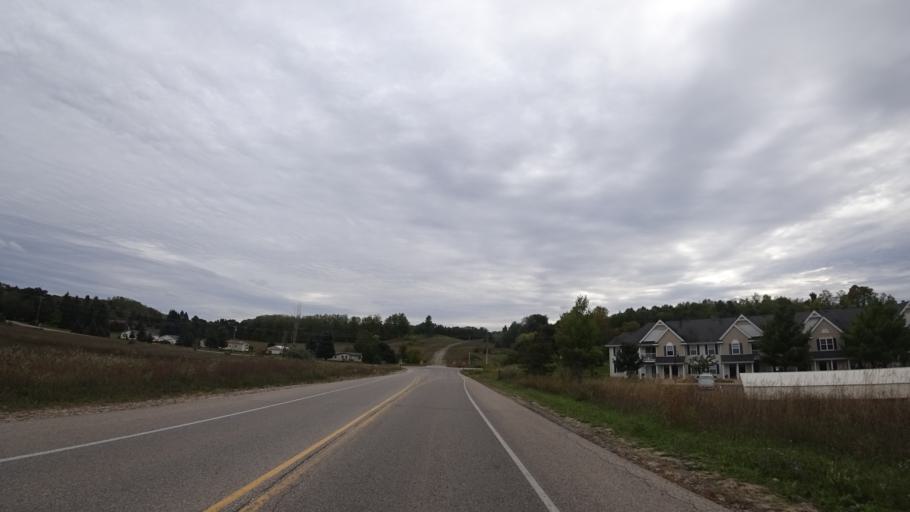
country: US
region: Michigan
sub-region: Emmet County
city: Petoskey
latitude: 45.3423
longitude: -84.9709
